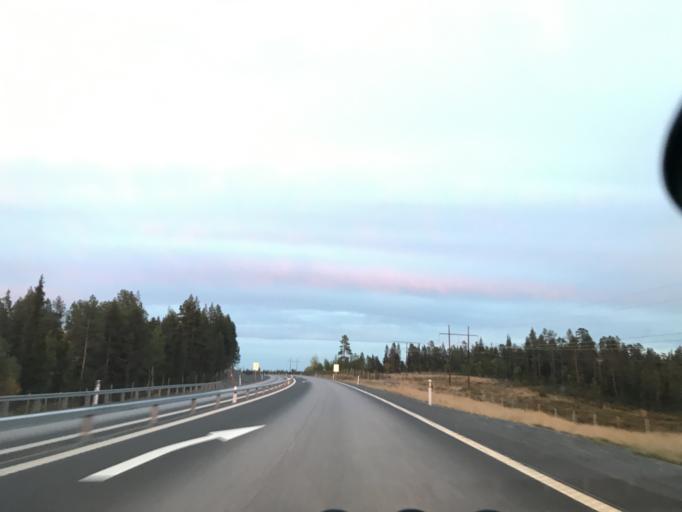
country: SE
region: Norrbotten
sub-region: Gallivare Kommun
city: Malmberget
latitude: 67.6732
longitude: 20.9114
